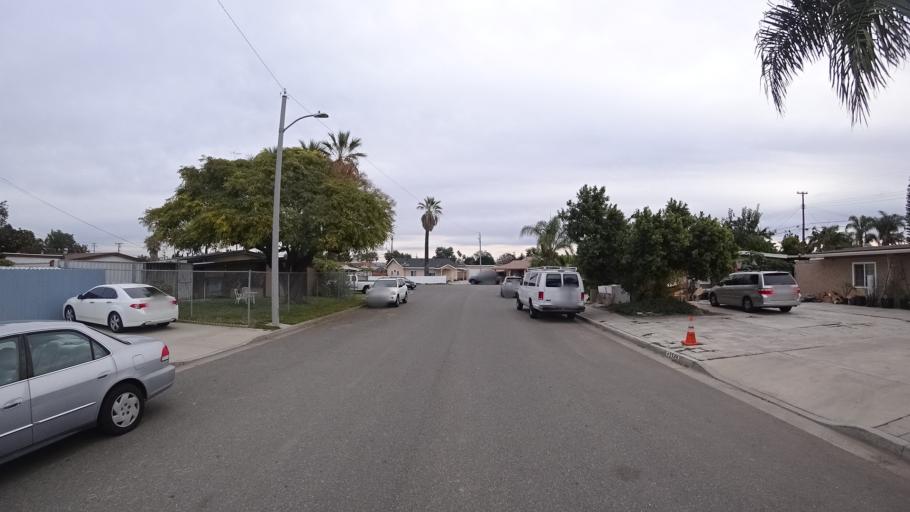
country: US
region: California
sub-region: Orange County
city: Garden Grove
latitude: 33.7692
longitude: -117.9367
